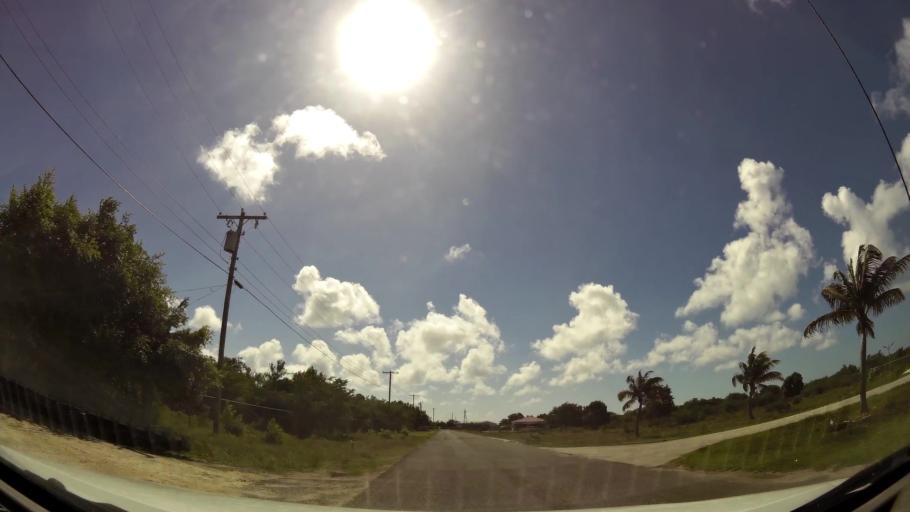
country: AG
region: Barbuda
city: Codrington
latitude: 17.6275
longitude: -61.8271
